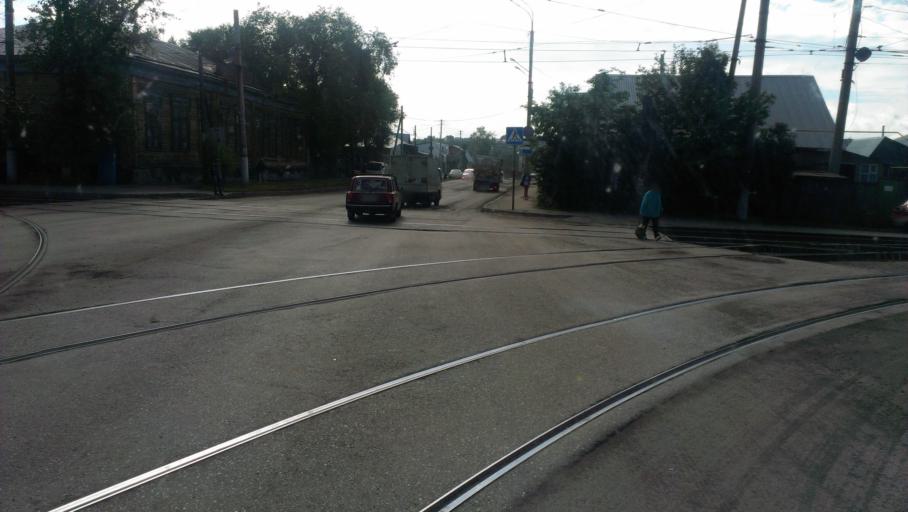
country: RU
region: Altai Krai
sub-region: Gorod Barnaulskiy
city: Barnaul
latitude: 53.3272
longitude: 83.7632
